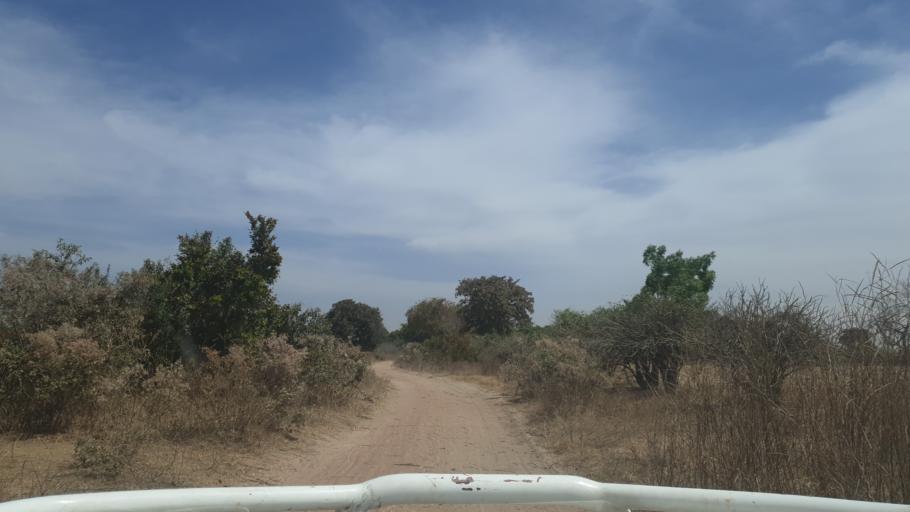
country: ML
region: Sikasso
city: Yorosso
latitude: 12.2841
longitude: -4.6826
